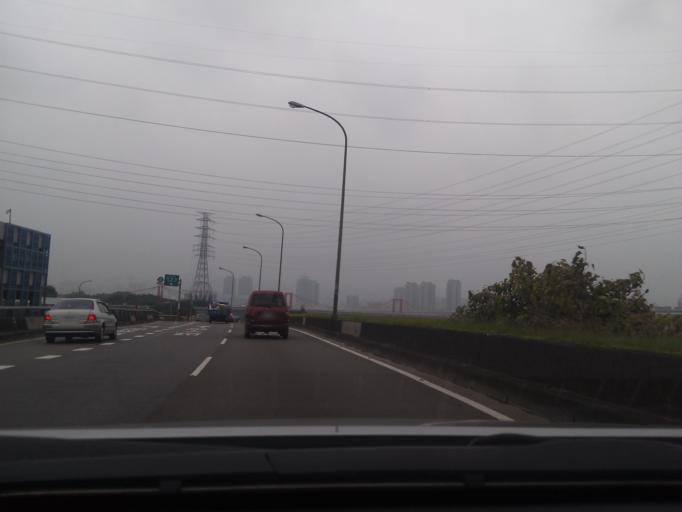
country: TW
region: Taipei
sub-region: Taipei
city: Banqiao
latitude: 25.0301
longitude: 121.4882
